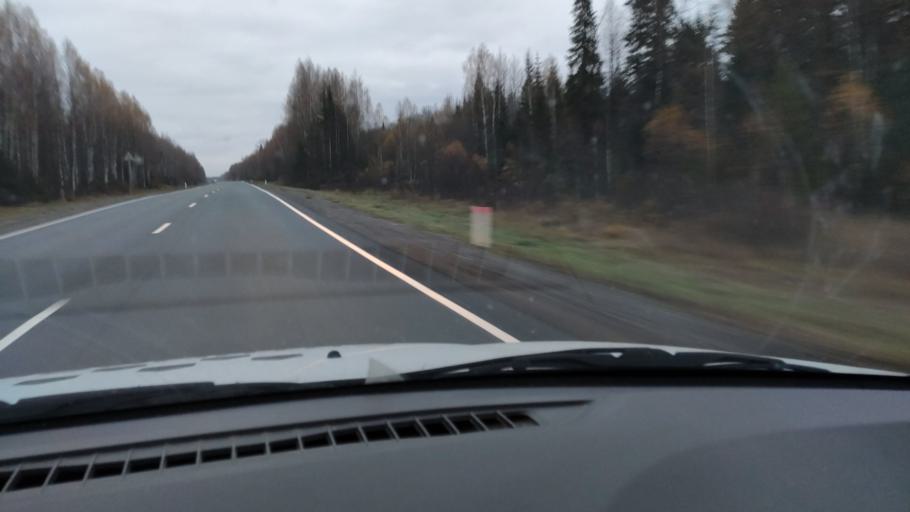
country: RU
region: Kirov
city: Kostino
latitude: 58.8311
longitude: 53.0219
